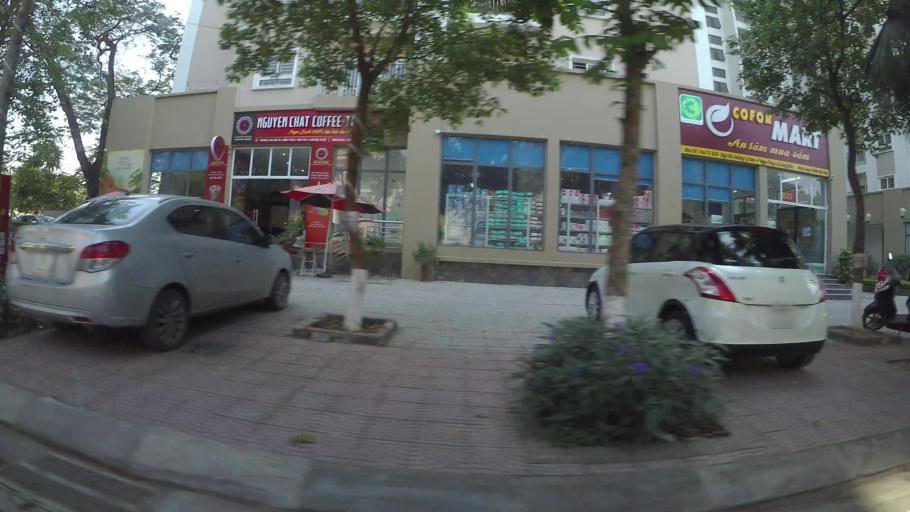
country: VN
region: Ha Noi
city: Hoan Kiem
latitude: 21.0648
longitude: 105.8790
